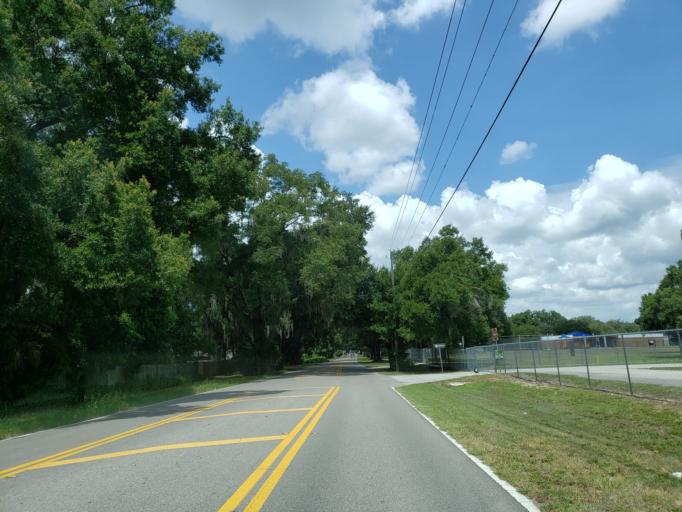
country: US
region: Florida
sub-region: Hillsborough County
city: Seffner
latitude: 27.9962
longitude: -82.2790
